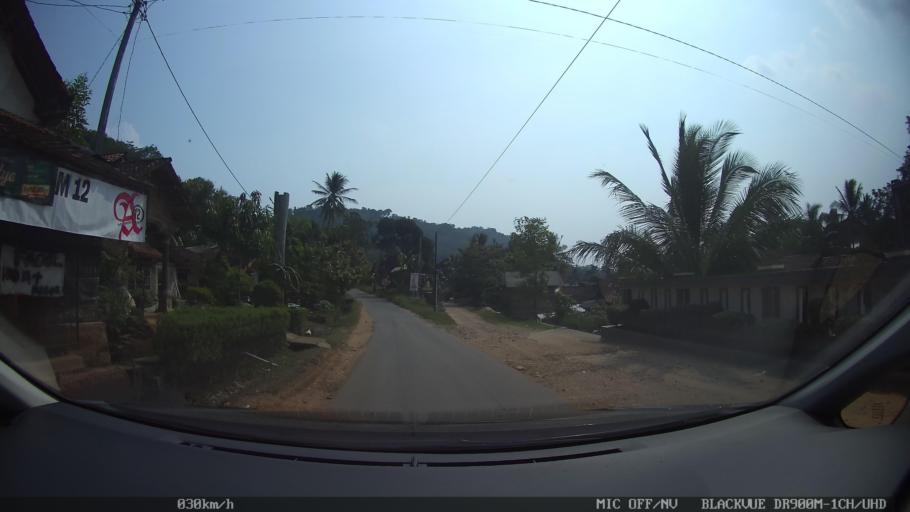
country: ID
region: Lampung
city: Pringsewu
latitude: -5.3830
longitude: 104.9952
